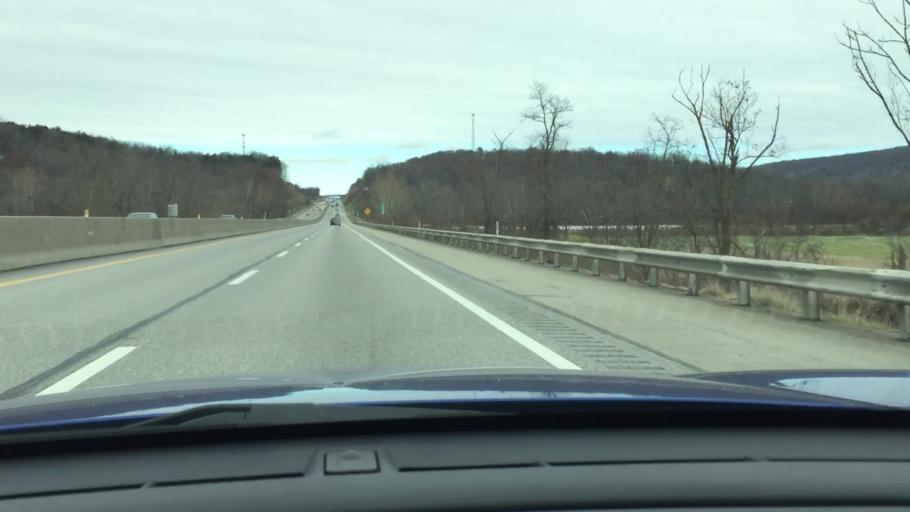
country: US
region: Pennsylvania
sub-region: Bedford County
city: Bedford
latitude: 40.0189
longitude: -78.5854
